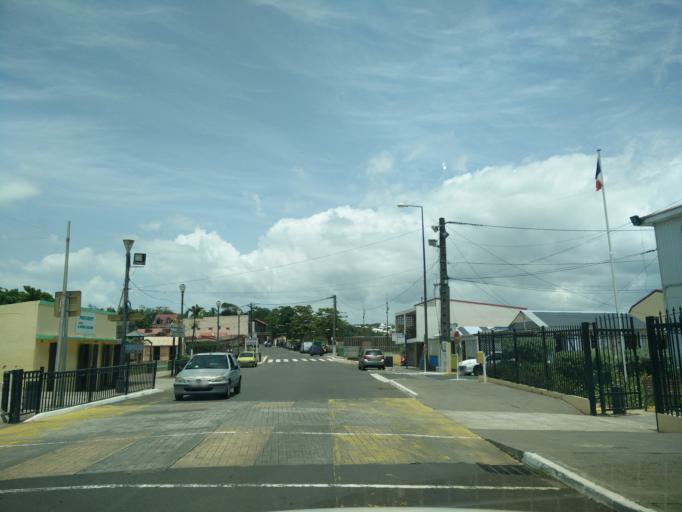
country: GP
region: Guadeloupe
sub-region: Guadeloupe
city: Petit-Bourg
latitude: 16.1914
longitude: -61.5908
